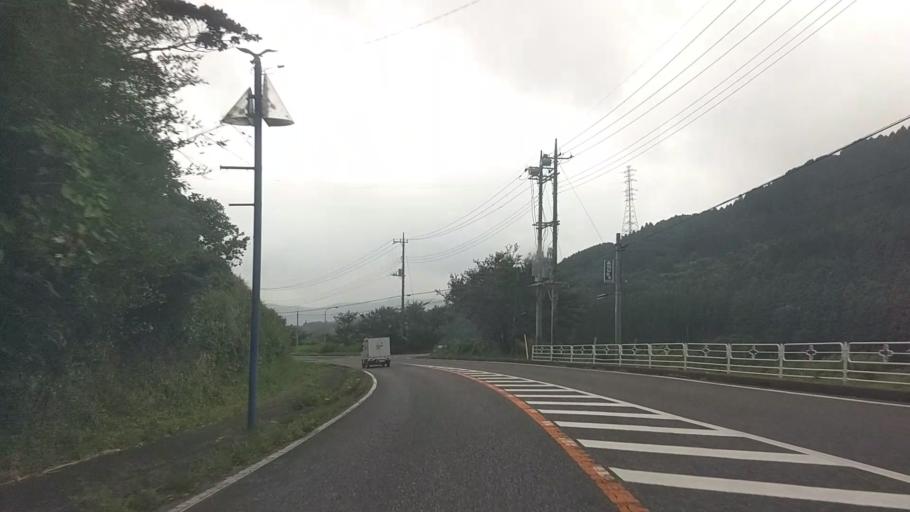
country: JP
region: Chiba
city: Kawaguchi
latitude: 35.1423
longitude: 140.0691
